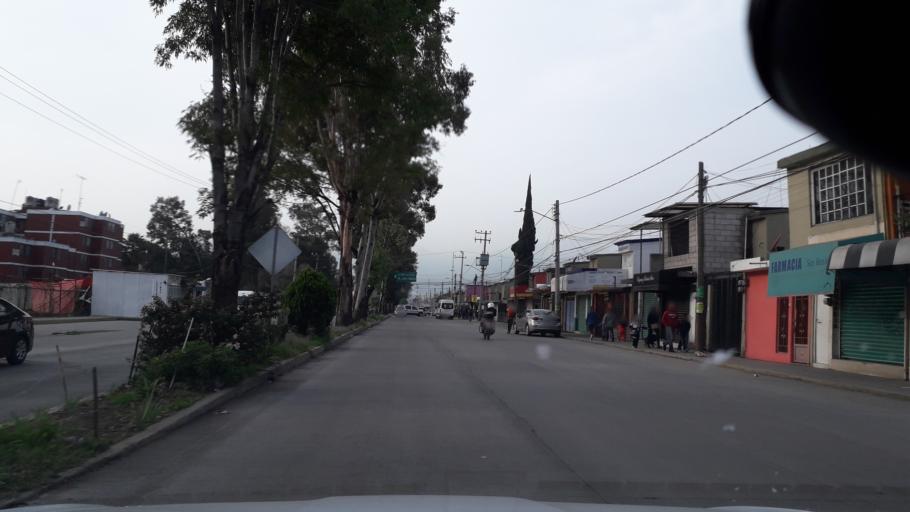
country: MX
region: Mexico
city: San Pablo de las Salinas
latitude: 19.6535
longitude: -99.0847
